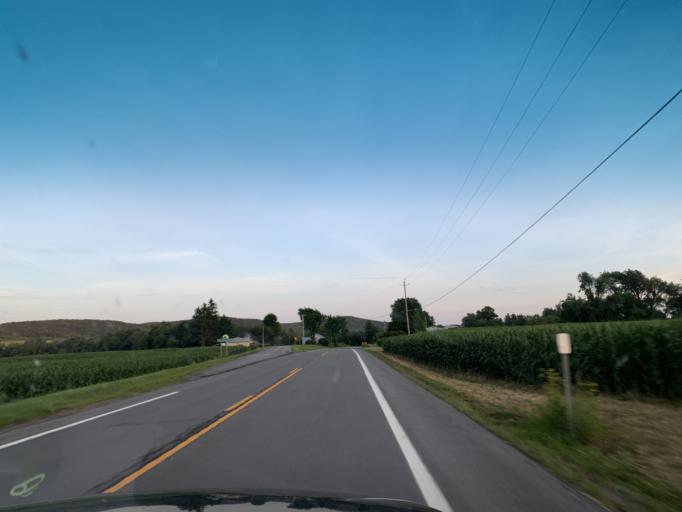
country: US
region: New York
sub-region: Oneida County
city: Chadwicks
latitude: 42.9153
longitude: -75.2419
